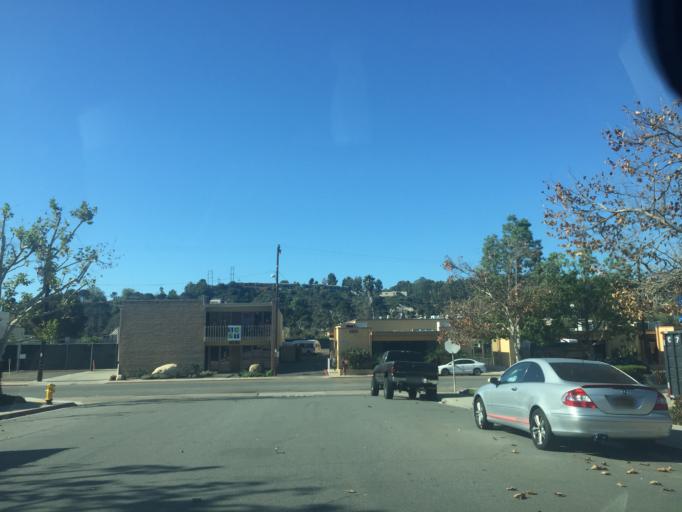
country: US
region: California
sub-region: San Diego County
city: La Mesa
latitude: 32.7888
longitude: -117.0991
